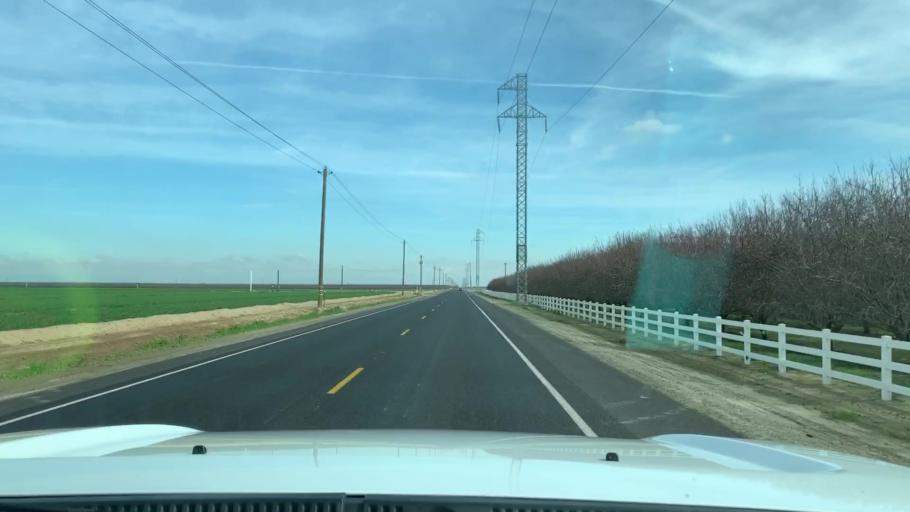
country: US
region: California
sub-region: Kern County
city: Shafter
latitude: 35.4420
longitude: -119.3436
